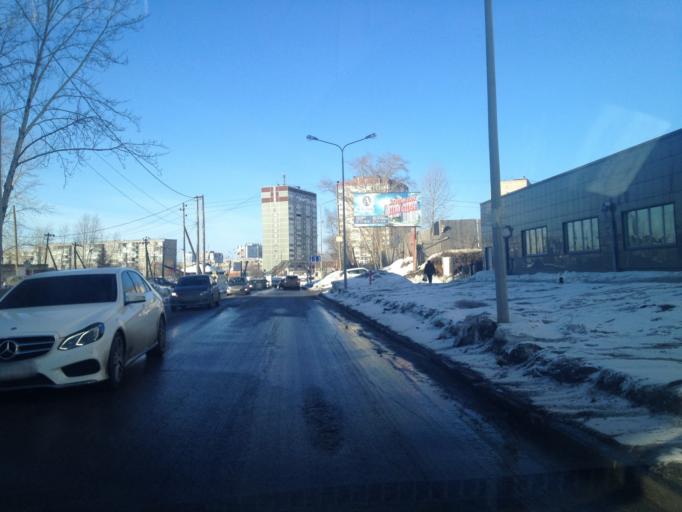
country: RU
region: Sverdlovsk
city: Sovkhoznyy
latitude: 56.8236
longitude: 60.5514
